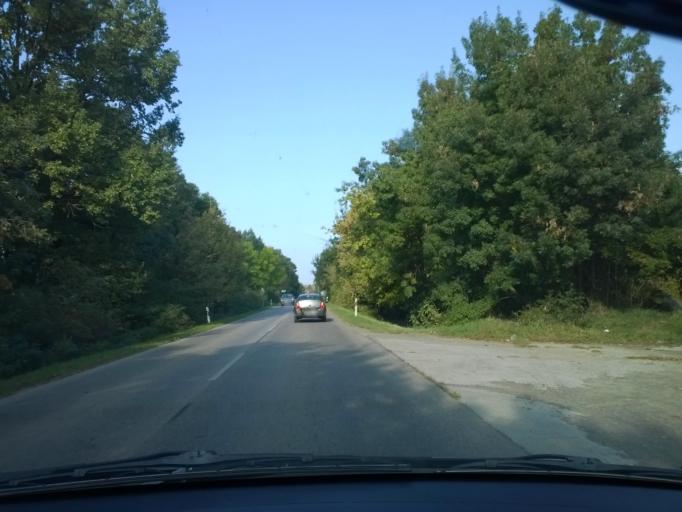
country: HU
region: Bacs-Kiskun
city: Kalocsa
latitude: 46.5156
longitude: 19.0002
